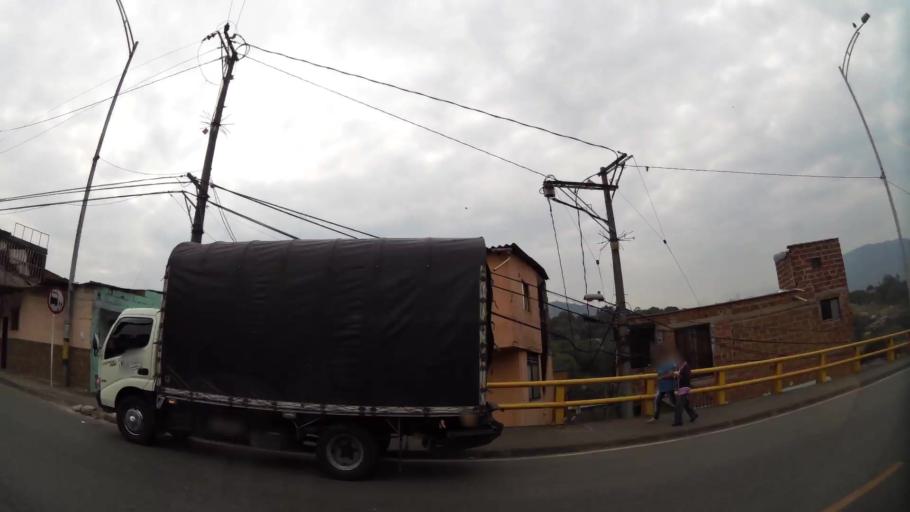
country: CO
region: Antioquia
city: Medellin
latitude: 6.2896
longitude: -75.5637
